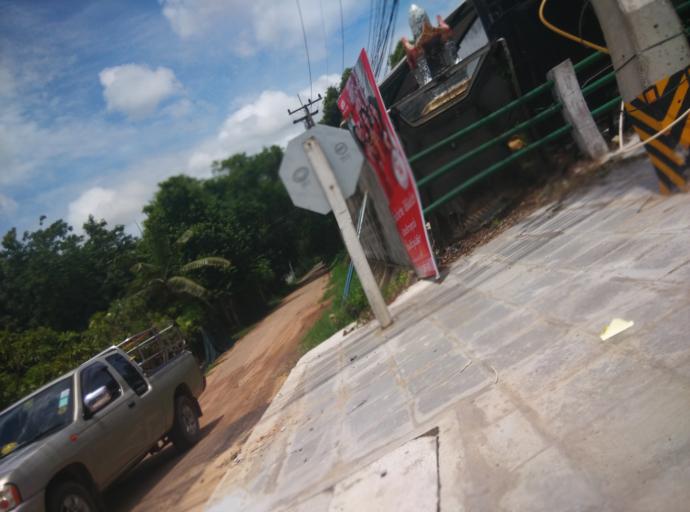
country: TH
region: Sisaket
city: Si Sa Ket
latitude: 15.1097
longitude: 104.3608
